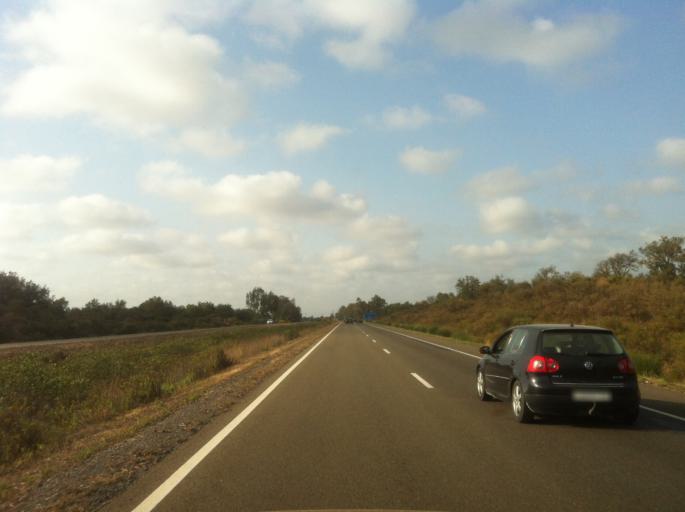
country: MA
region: Gharb-Chrarda-Beni Hssen
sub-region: Kenitra Province
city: Kenitra
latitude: 34.2243
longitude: -6.5474
